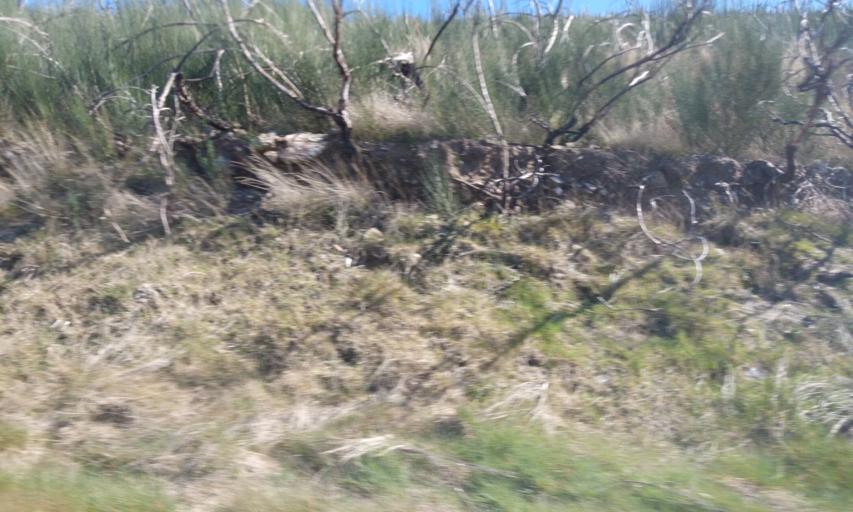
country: PT
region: Guarda
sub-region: Manteigas
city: Manteigas
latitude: 40.4904
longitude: -7.5500
